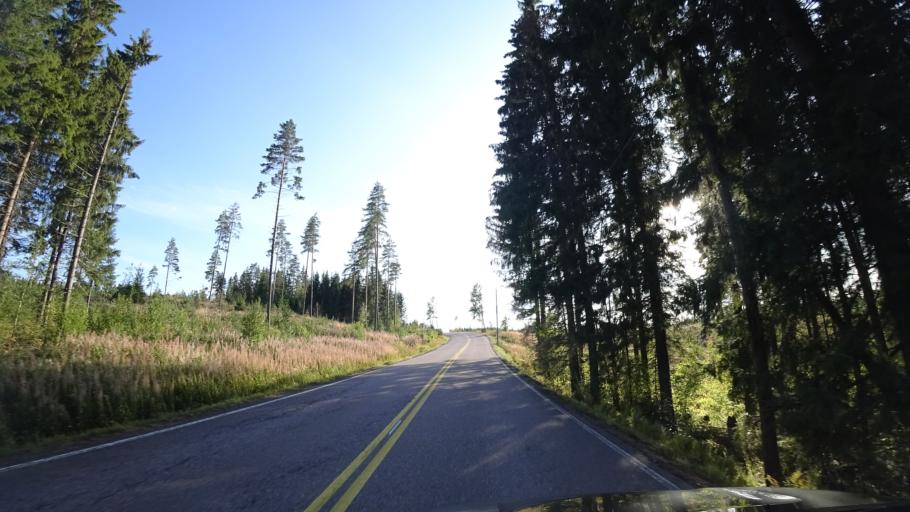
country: FI
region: Paijanne Tavastia
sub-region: Lahti
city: Hollola
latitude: 61.1673
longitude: 25.3653
